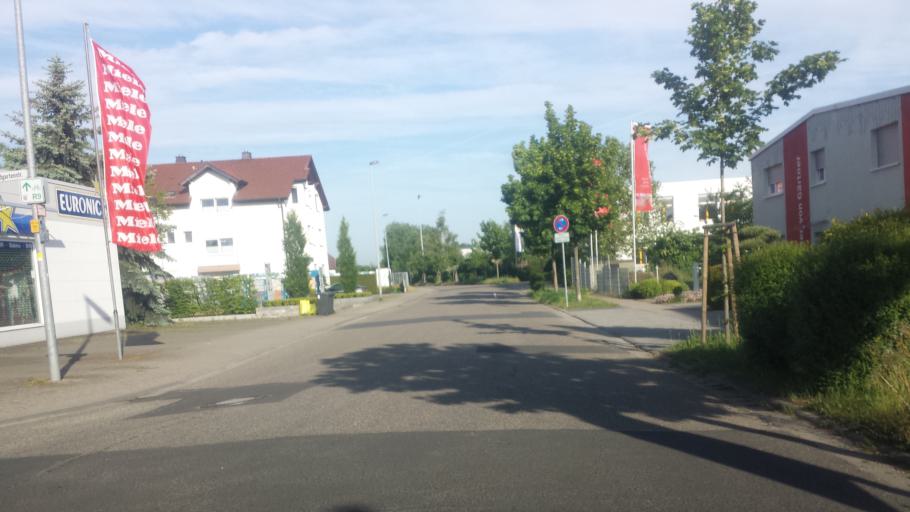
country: DE
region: Hesse
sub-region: Regierungsbezirk Darmstadt
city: Burstadt
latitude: 49.6494
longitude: 8.4685
